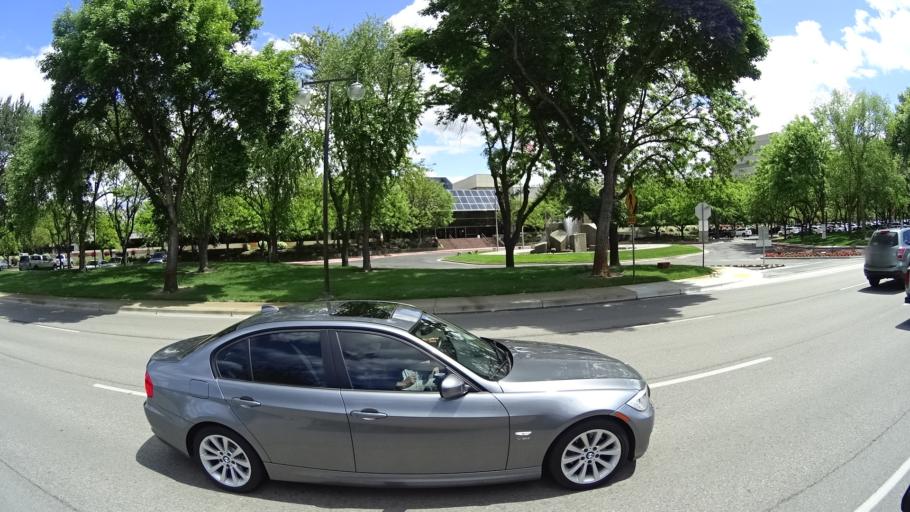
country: US
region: Idaho
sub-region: Ada County
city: Boise
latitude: 43.6048
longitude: -116.1917
